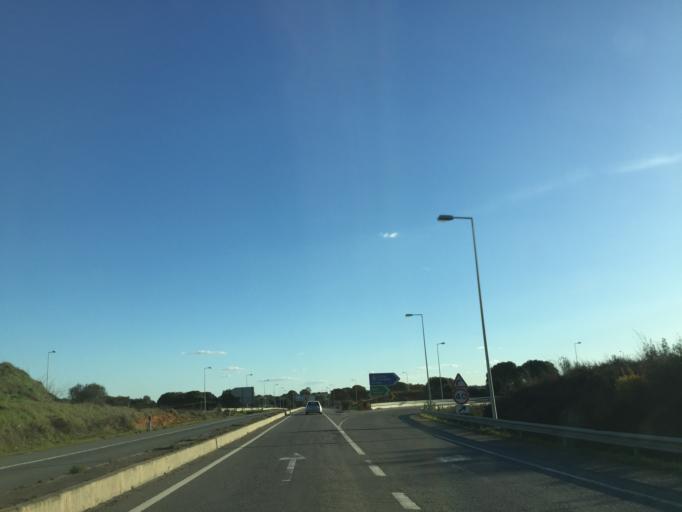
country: PT
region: Setubal
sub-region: Grandola
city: Grandola
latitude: 38.1128
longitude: -8.4183
